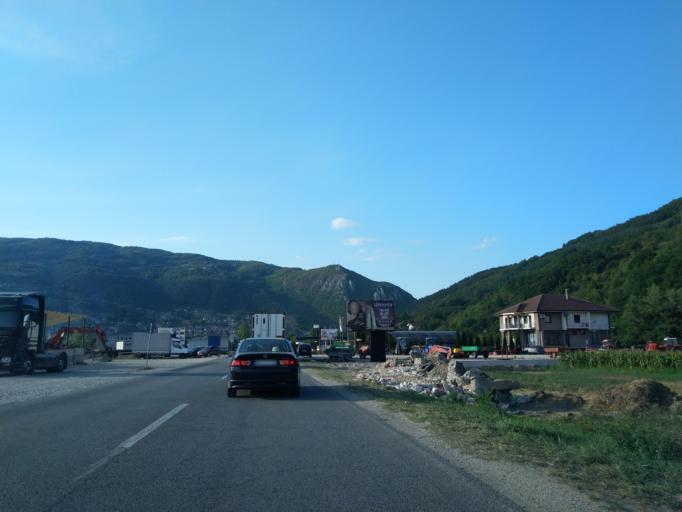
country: RS
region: Central Serbia
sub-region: Zlatiborski Okrug
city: Prijepolje
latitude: 43.3633
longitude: 19.6363
